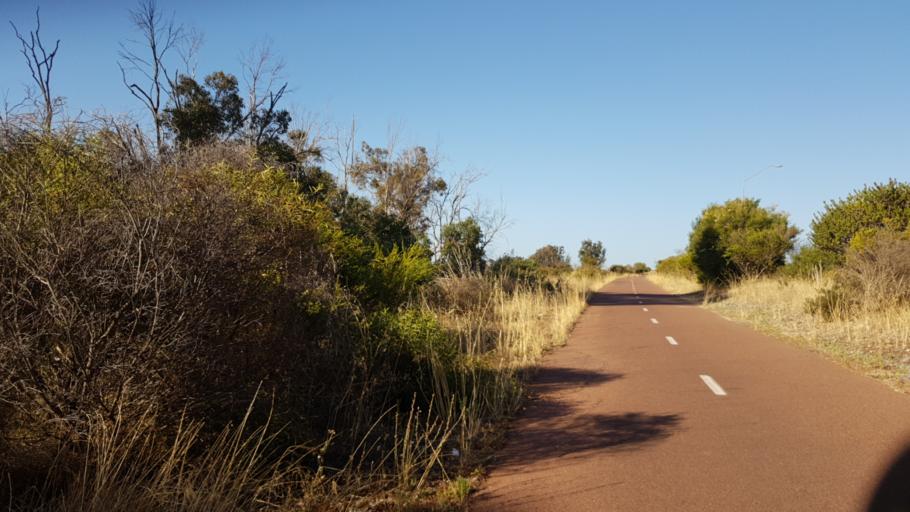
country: AU
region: Western Australia
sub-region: Kwinana
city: Wellard
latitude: -32.2752
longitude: 115.8414
